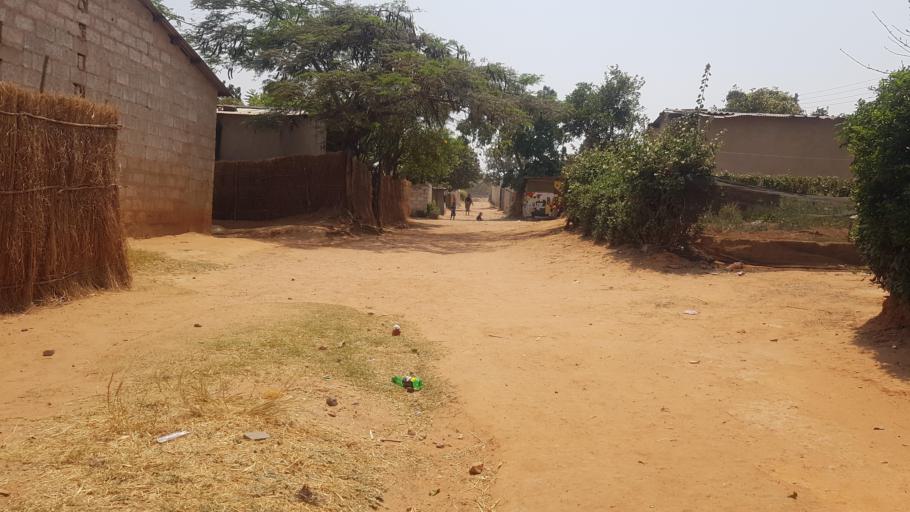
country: ZM
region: Lusaka
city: Lusaka
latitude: -15.4382
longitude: 28.3809
